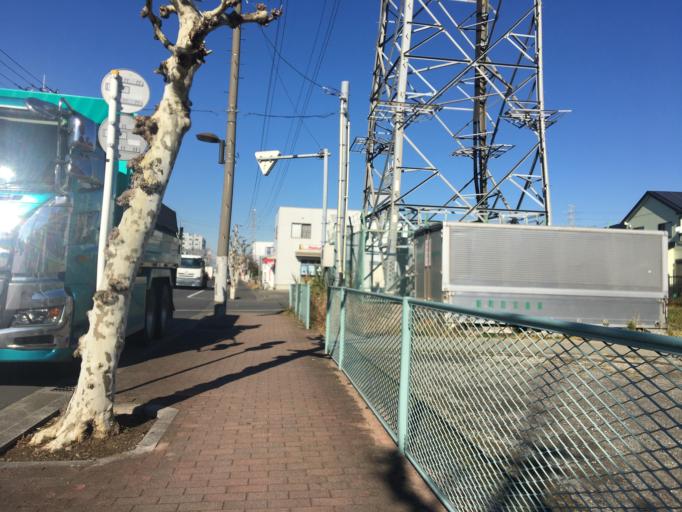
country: JP
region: Saitama
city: Yashio-shi
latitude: 35.8338
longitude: 139.8315
